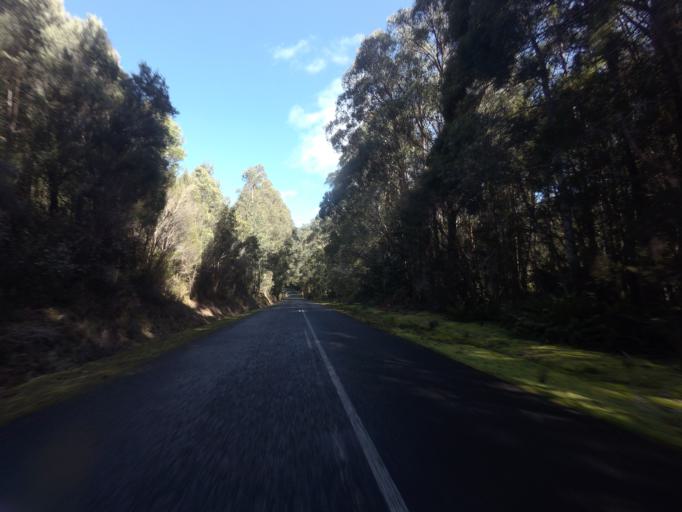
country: AU
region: Tasmania
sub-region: Derwent Valley
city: New Norfolk
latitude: -42.7684
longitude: 146.5680
